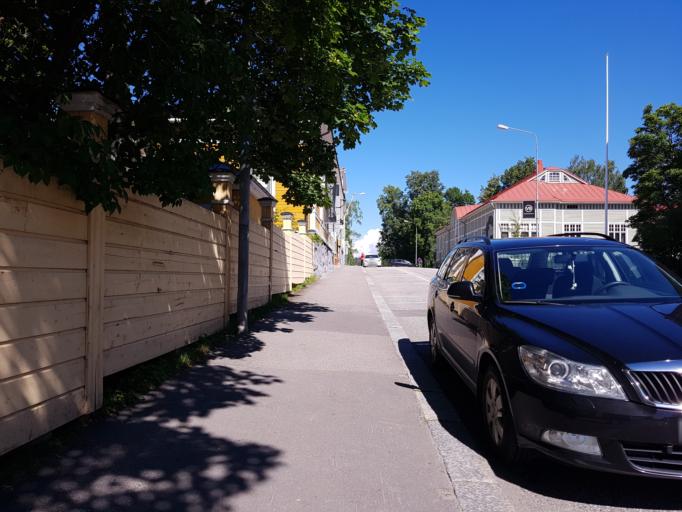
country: FI
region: Northern Savo
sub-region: Kuopio
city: Kuopio
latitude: 62.8901
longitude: 27.6857
